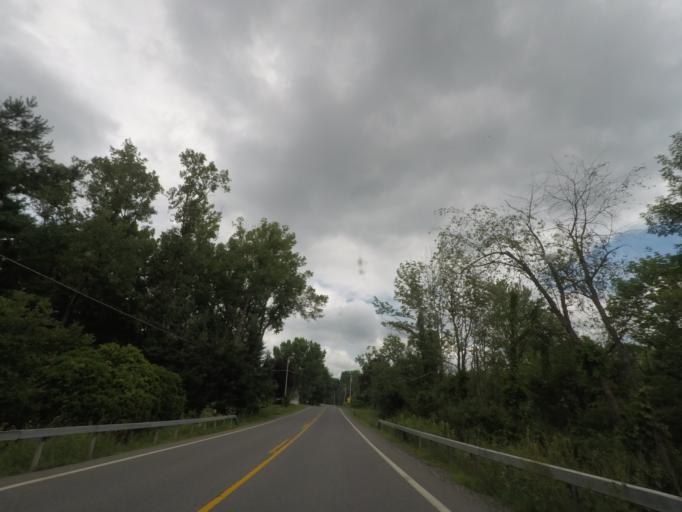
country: US
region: New York
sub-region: Saratoga County
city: Stillwater
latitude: 42.9997
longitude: -73.7093
